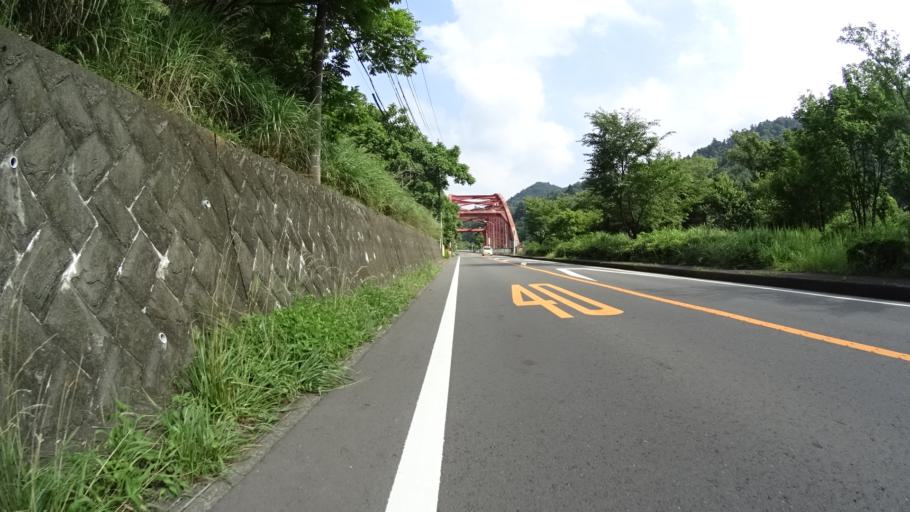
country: JP
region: Kanagawa
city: Atsugi
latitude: 35.5104
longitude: 139.2497
